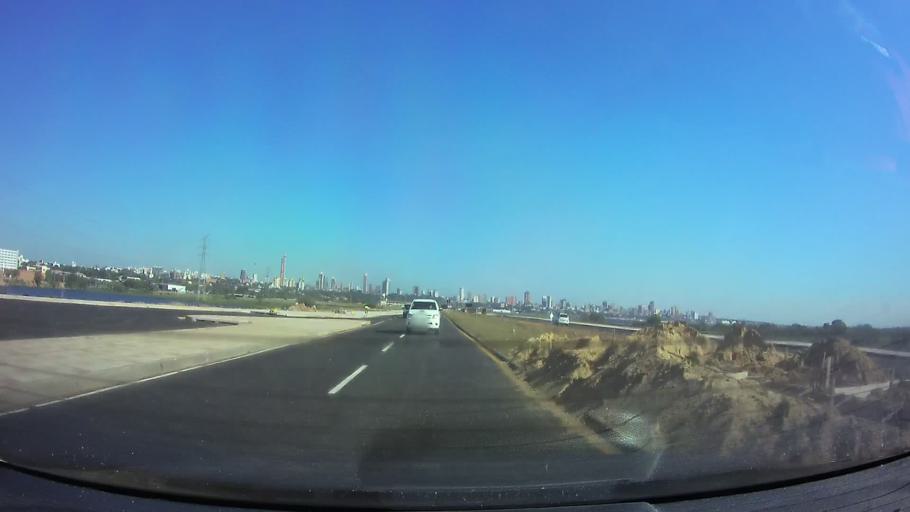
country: PY
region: Asuncion
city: Asuncion
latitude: -25.2655
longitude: -57.6094
